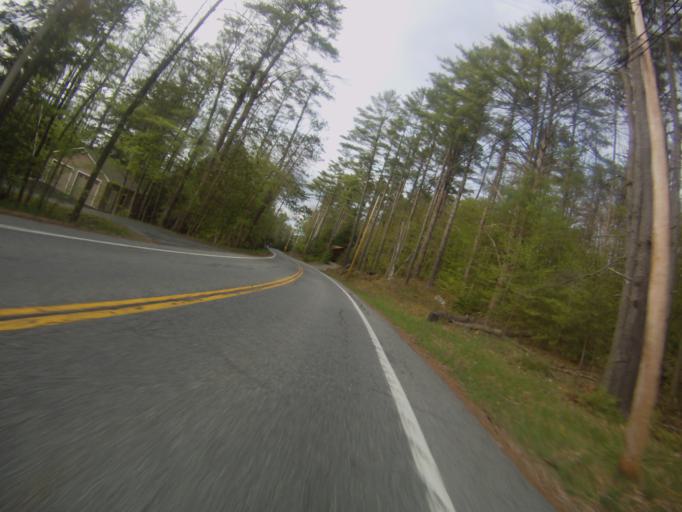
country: US
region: New York
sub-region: Warren County
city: Warrensburg
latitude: 43.7236
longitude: -73.6834
